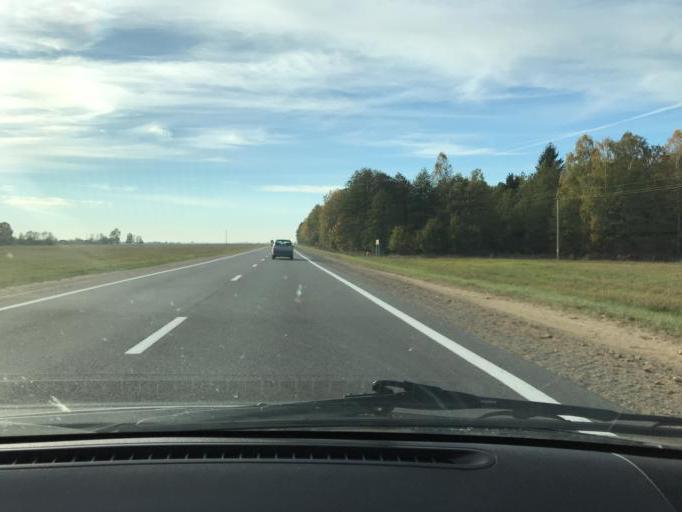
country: BY
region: Brest
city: Ivanava
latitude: 52.1561
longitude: 25.7050
